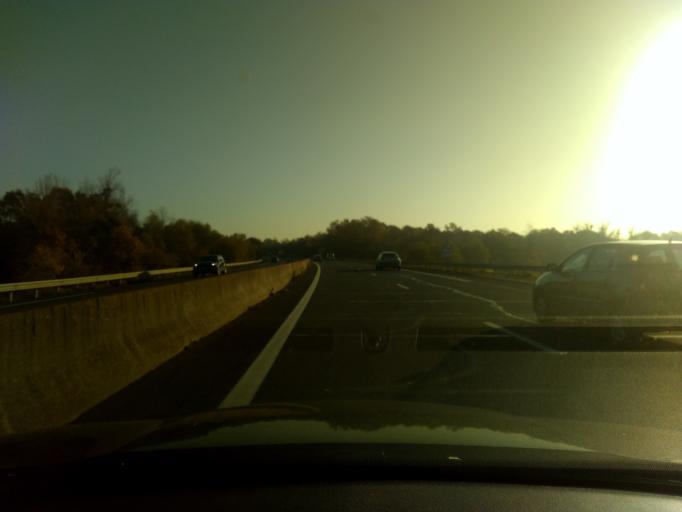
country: FR
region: Lorraine
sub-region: Departement de la Moselle
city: Marly
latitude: 49.0509
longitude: 6.1619
